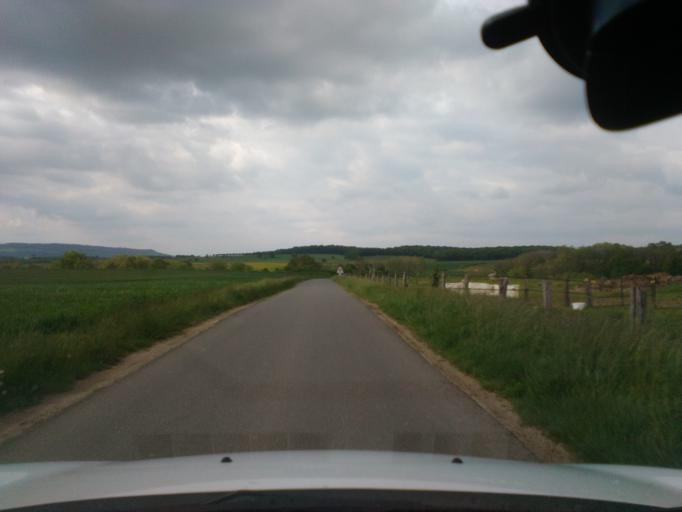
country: FR
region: Lorraine
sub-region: Departement des Vosges
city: Mirecourt
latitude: 48.3397
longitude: 6.1011
